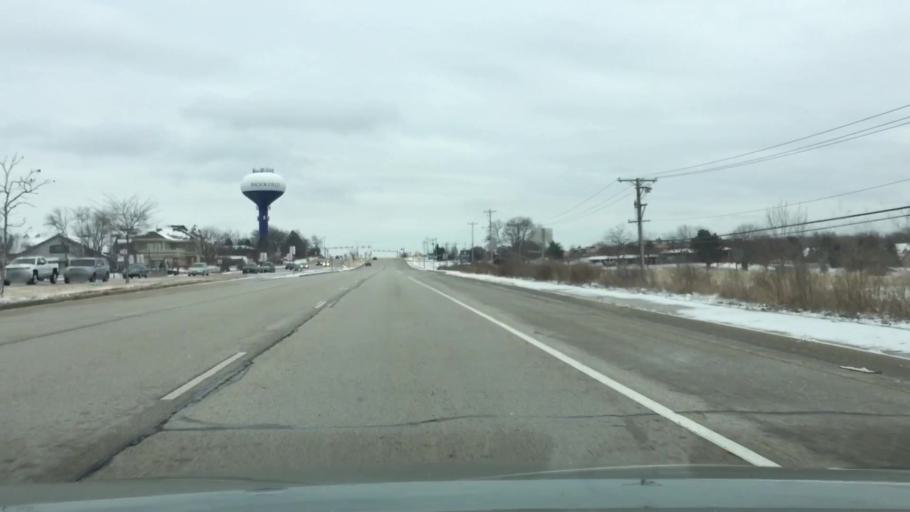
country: US
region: Wisconsin
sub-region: Waukesha County
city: Brookfield
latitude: 43.0902
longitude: -88.1330
